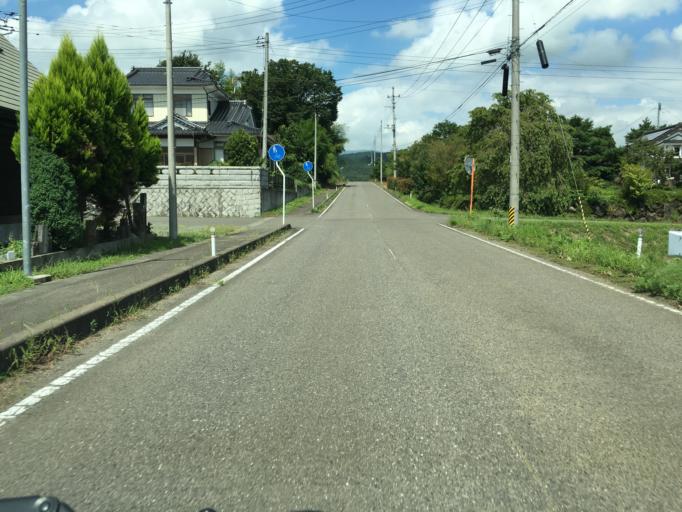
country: JP
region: Fukushima
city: Motomiya
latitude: 37.5480
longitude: 140.3780
